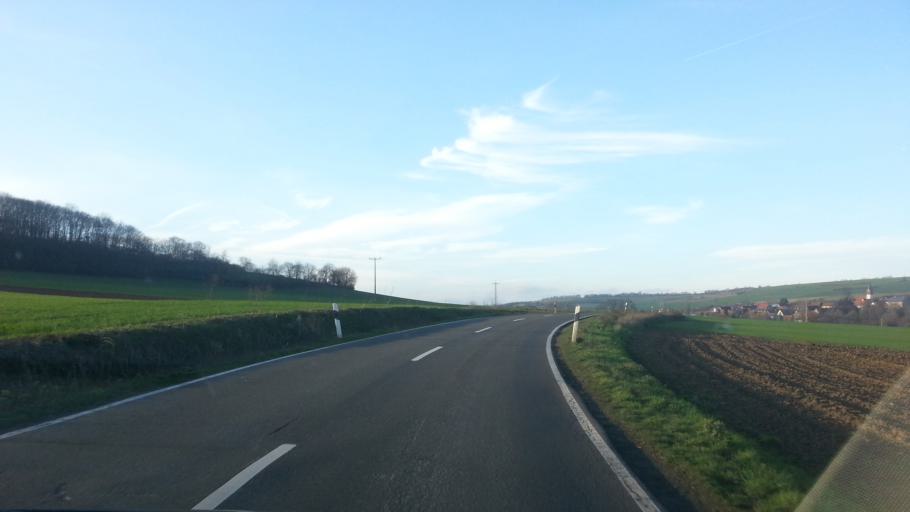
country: DE
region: Rheinland-Pfalz
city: Gauersheim
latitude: 49.6615
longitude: 8.0666
